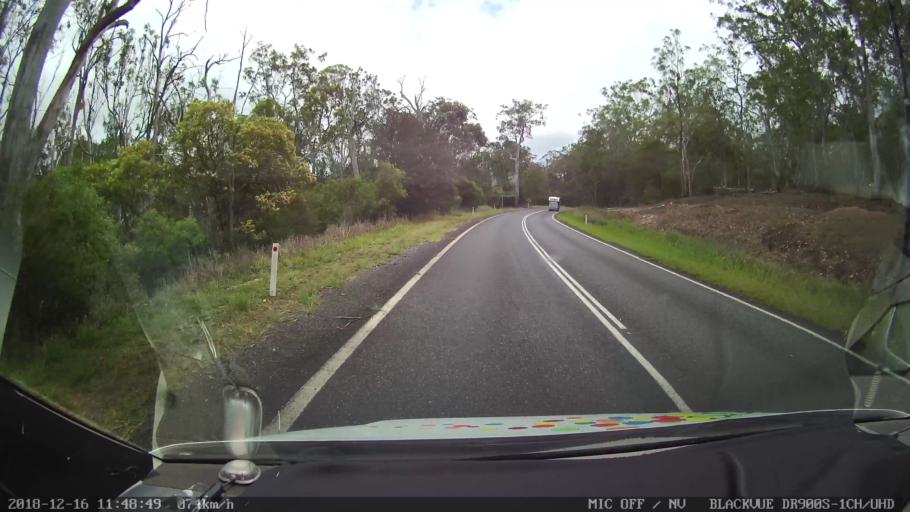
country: AU
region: New South Wales
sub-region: Tenterfield Municipality
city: Carrolls Creek
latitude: -28.9185
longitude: 152.2503
